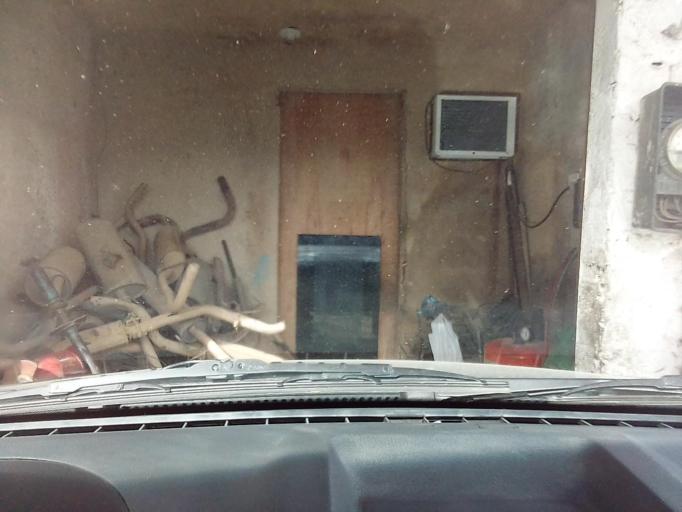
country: BR
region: Pernambuco
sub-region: Vitoria De Santo Antao
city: Vitoria de Santo Antao
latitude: -8.1174
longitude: -35.2981
